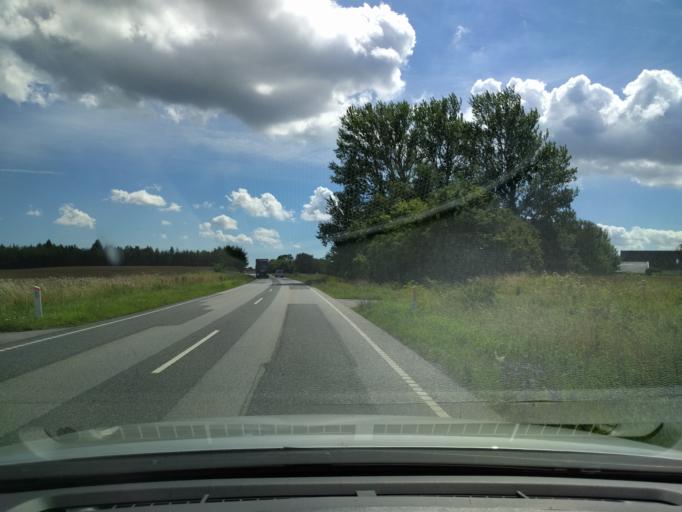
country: DK
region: Zealand
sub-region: Guldborgsund Kommune
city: Stubbekobing
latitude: 54.9365
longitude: 12.0021
